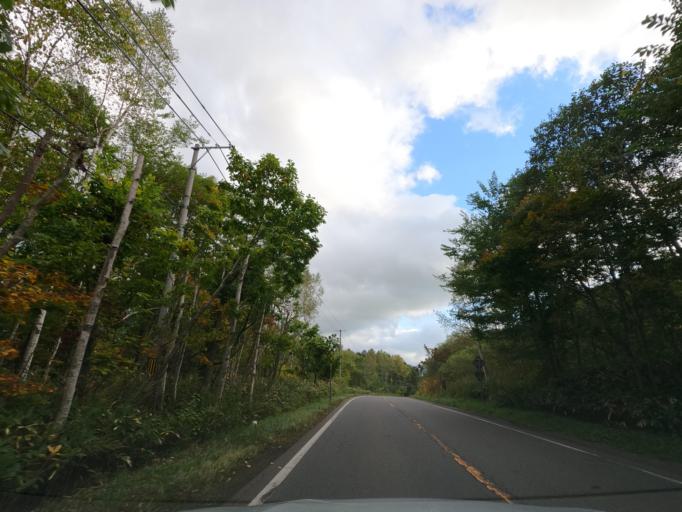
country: JP
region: Hokkaido
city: Date
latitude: 42.6588
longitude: 141.0686
